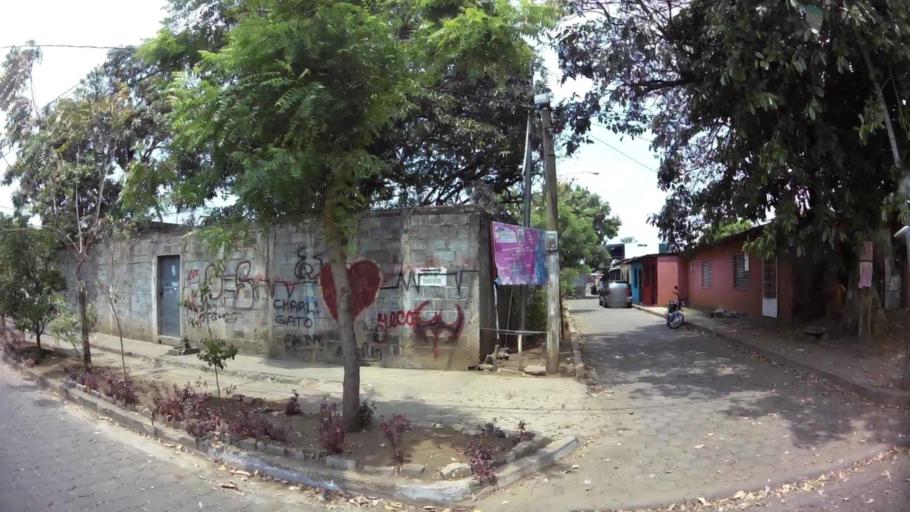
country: NI
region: Managua
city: Ciudad Sandino
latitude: 12.1559
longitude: -86.2998
